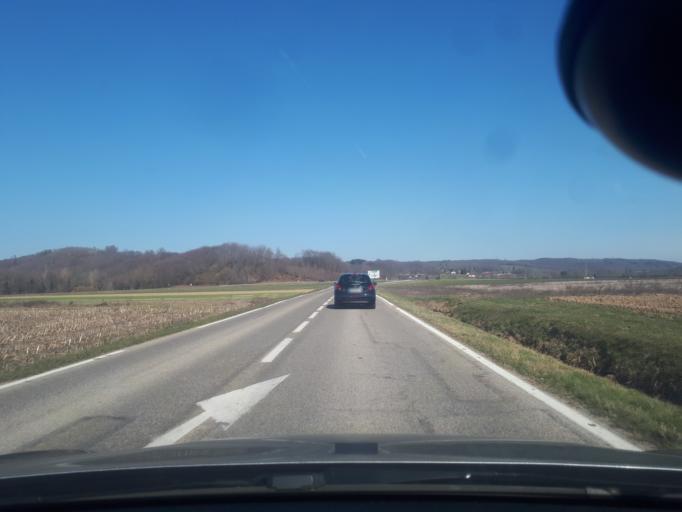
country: FR
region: Rhone-Alpes
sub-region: Departement de l'Isere
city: Champier
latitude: 45.4349
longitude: 5.2829
